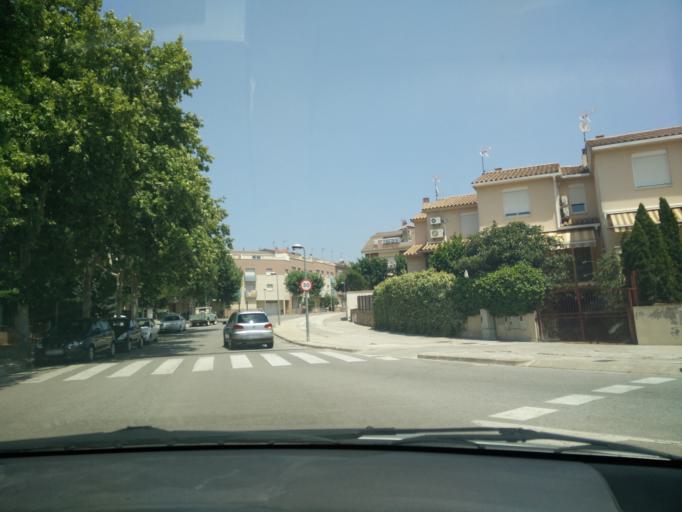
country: ES
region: Catalonia
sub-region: Provincia de Barcelona
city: Manresa
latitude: 41.7179
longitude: 1.8430
